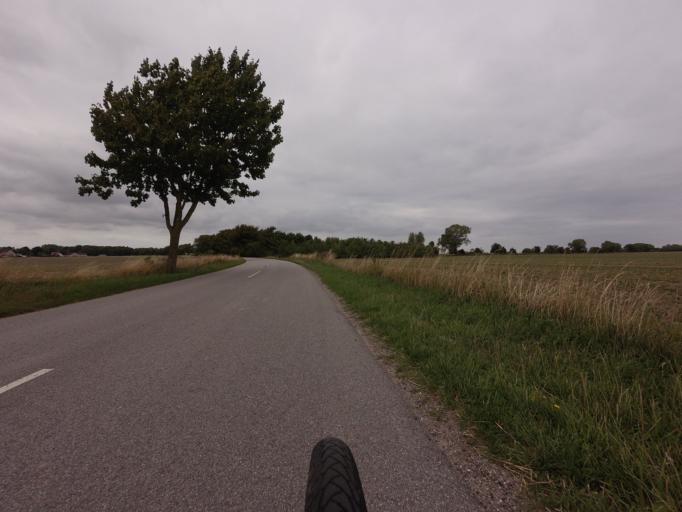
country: DK
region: Zealand
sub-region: Stevns Kommune
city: Store Heddinge
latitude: 55.2923
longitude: 12.4459
